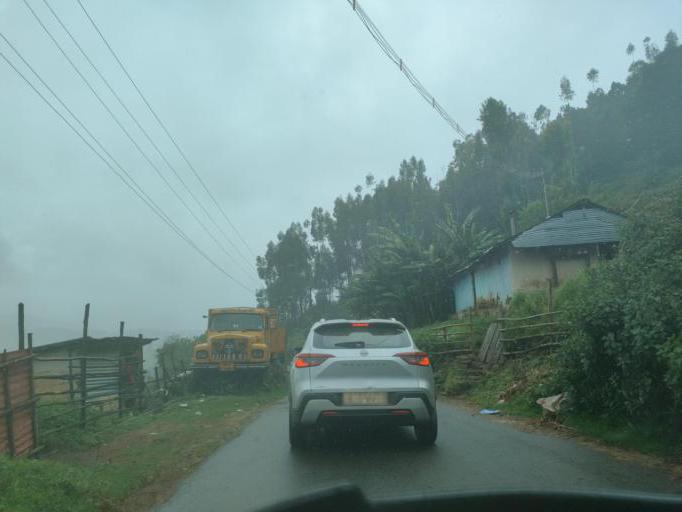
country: IN
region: Tamil Nadu
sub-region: Dindigul
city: Kodaikanal
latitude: 10.2367
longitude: 77.3497
